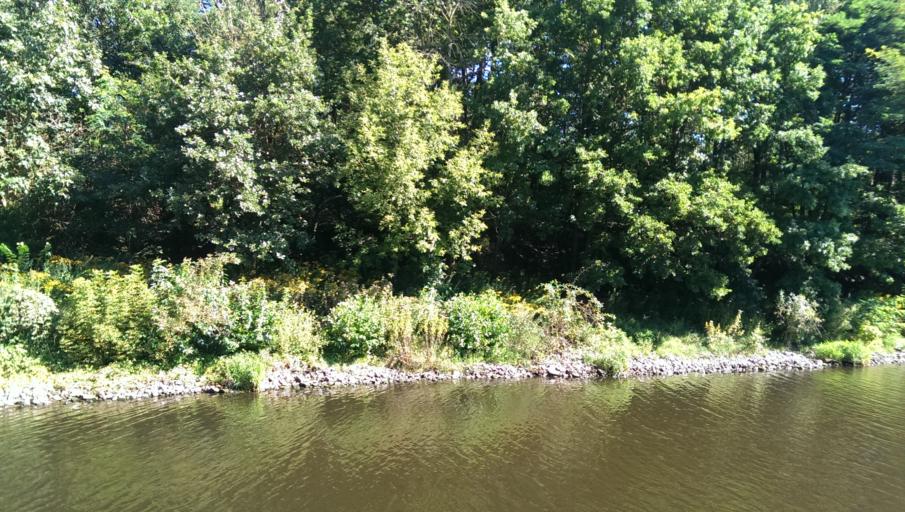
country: DE
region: Brandenburg
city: Stahnsdorf
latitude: 52.3978
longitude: 13.1924
